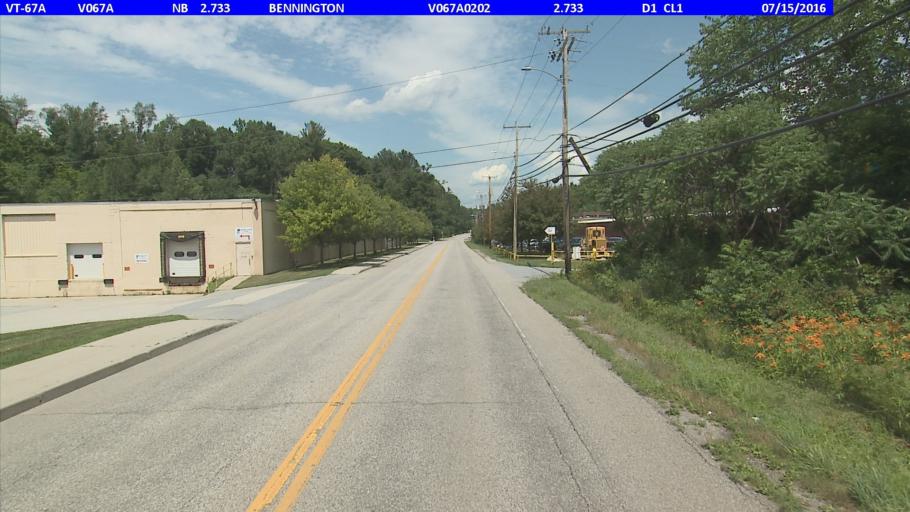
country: US
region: Vermont
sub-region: Bennington County
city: North Bennington
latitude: 42.9219
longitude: -73.2460
